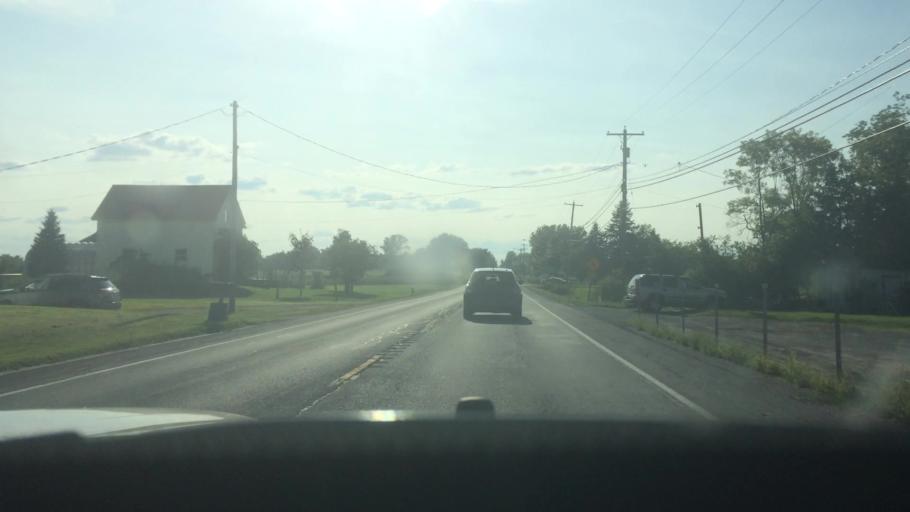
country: US
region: New York
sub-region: St. Lawrence County
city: Potsdam
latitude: 44.6700
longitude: -74.9560
